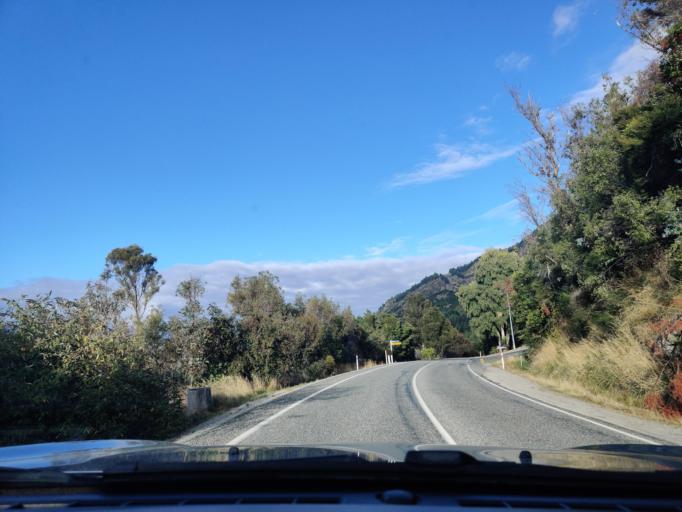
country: NZ
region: Otago
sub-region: Queenstown-Lakes District
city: Queenstown
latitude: -45.0462
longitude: 168.6302
